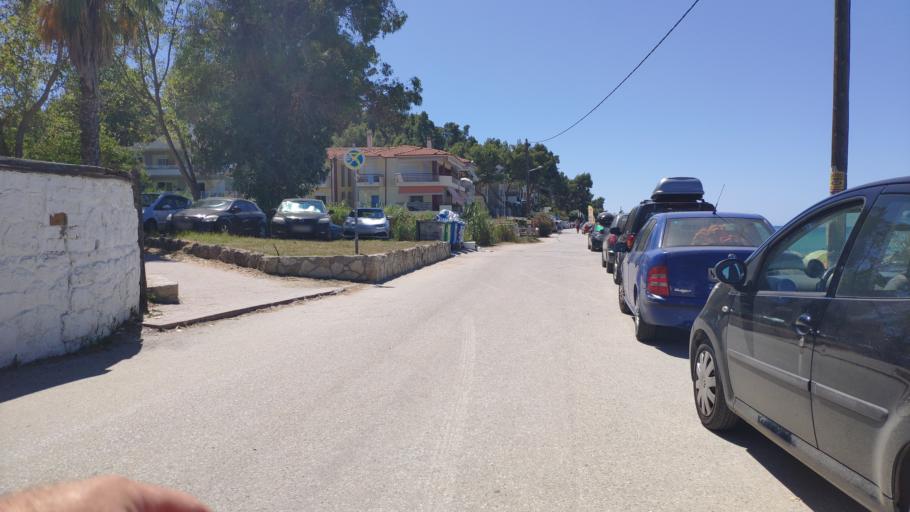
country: GR
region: Central Macedonia
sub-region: Nomos Chalkidikis
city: Kassandreia
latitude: 40.0340
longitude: 23.3602
